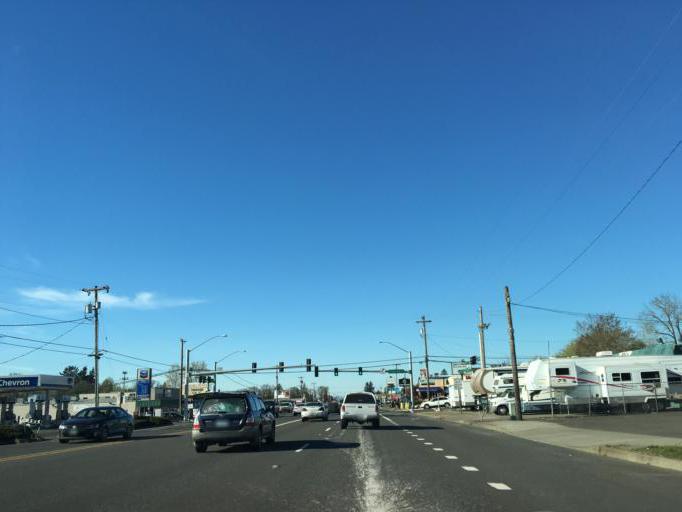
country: US
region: Oregon
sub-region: Clackamas County
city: Oak Grove
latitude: 45.4216
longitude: -122.6332
